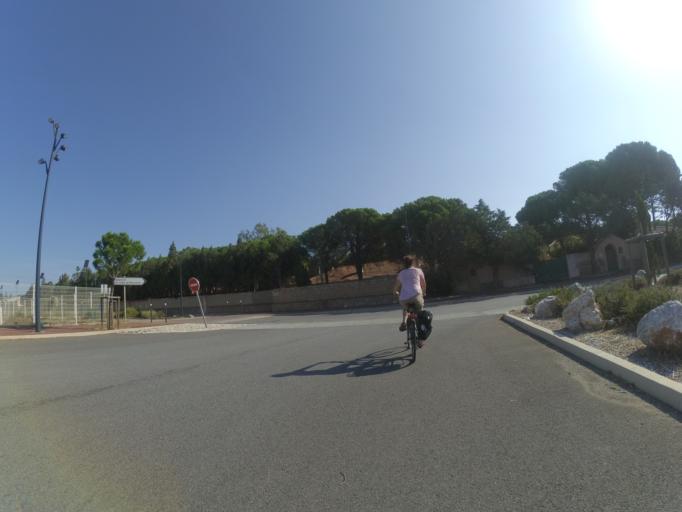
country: FR
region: Languedoc-Roussillon
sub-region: Departement des Pyrenees-Orientales
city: Salses-le-Chateau
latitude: 42.8036
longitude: 2.8932
